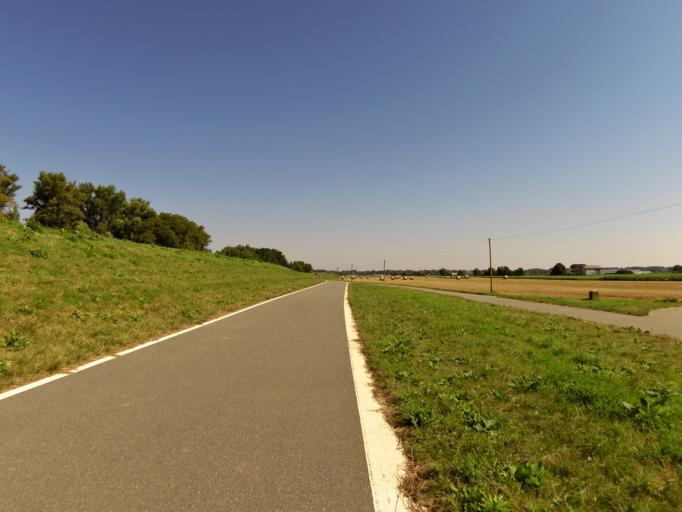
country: DE
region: Rheinland-Pfalz
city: Nackenheim
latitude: 49.9057
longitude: 8.3607
